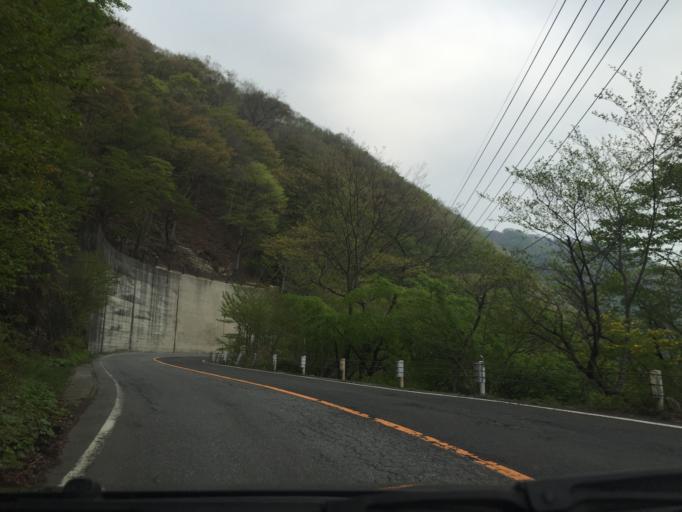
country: JP
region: Tochigi
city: Nikko
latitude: 36.9042
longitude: 139.7034
